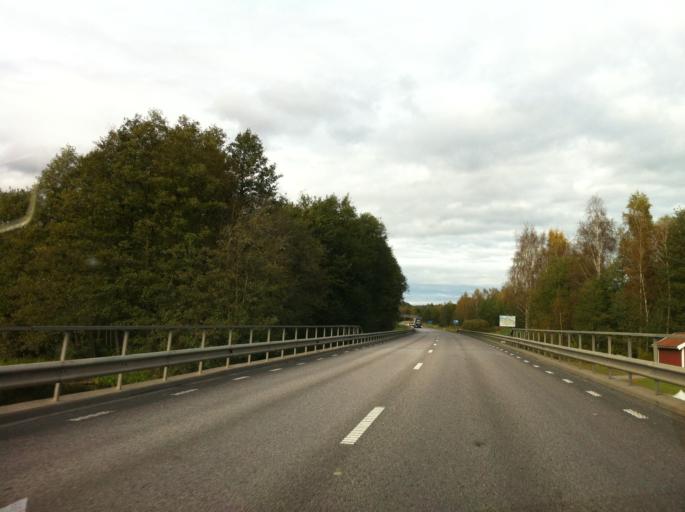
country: SE
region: OErebro
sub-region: Askersunds Kommun
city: Askersund
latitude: 58.8803
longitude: 14.8965
